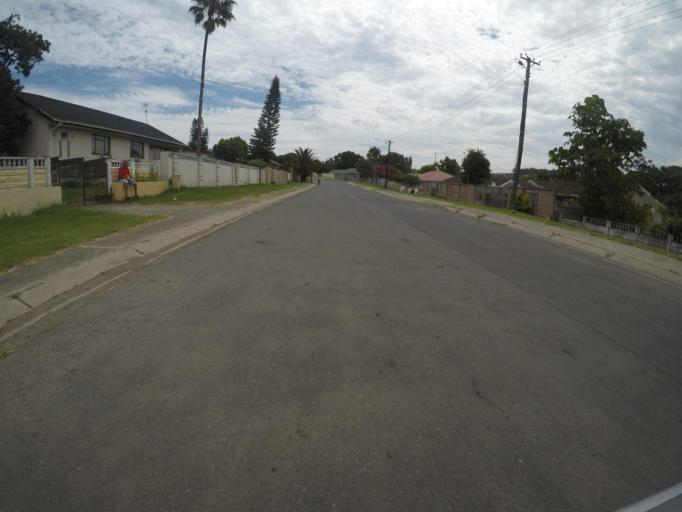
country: ZA
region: Eastern Cape
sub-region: Buffalo City Metropolitan Municipality
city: East London
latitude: -32.9945
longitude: 27.8762
